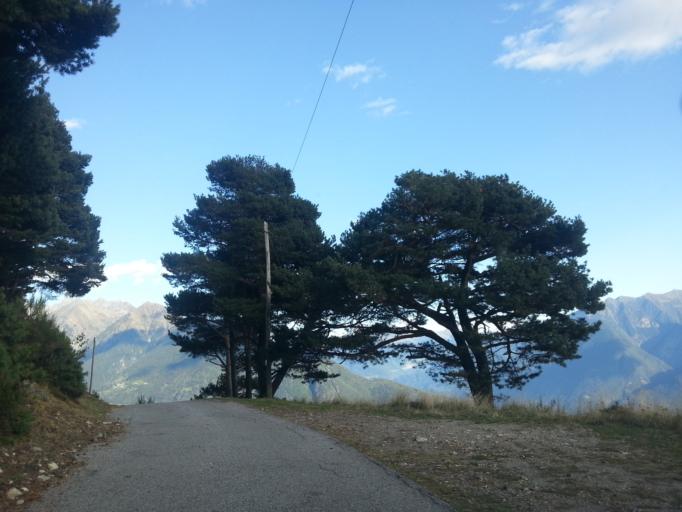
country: IT
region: Lombardy
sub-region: Provincia di Como
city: Sorico
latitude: 46.1924
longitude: 9.3903
